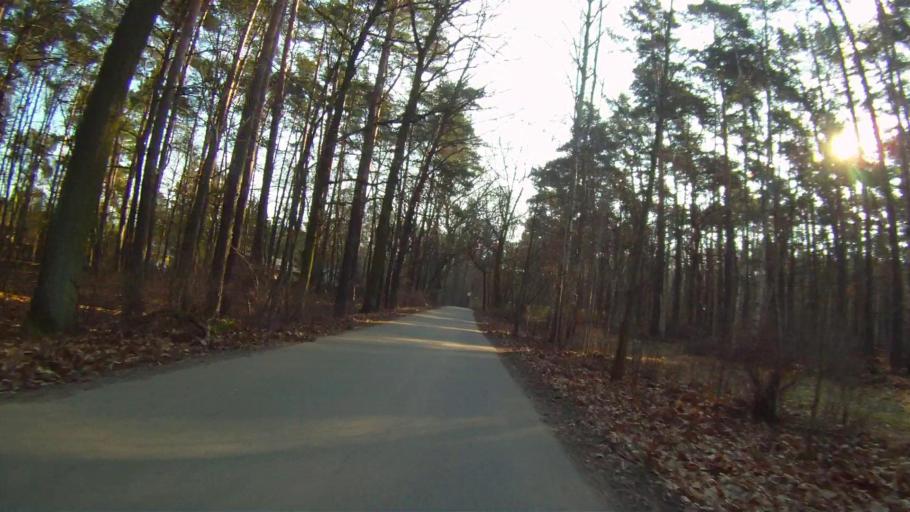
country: DE
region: Berlin
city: Rahnsdorf
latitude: 52.4222
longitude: 13.7016
